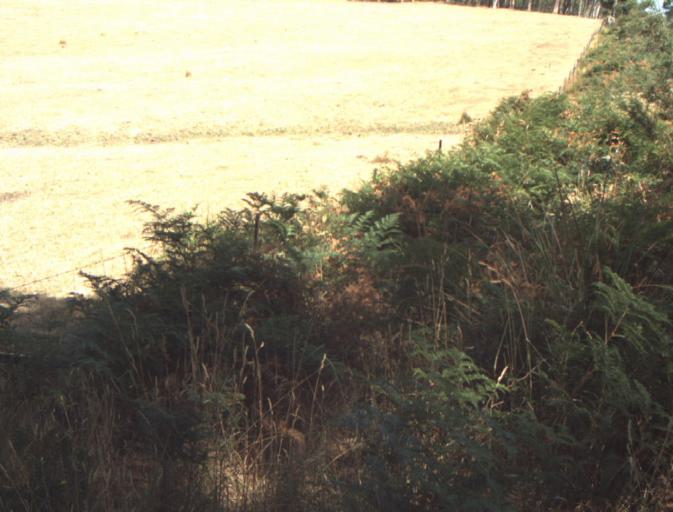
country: AU
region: Tasmania
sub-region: Launceston
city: Mayfield
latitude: -41.2492
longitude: 147.1664
